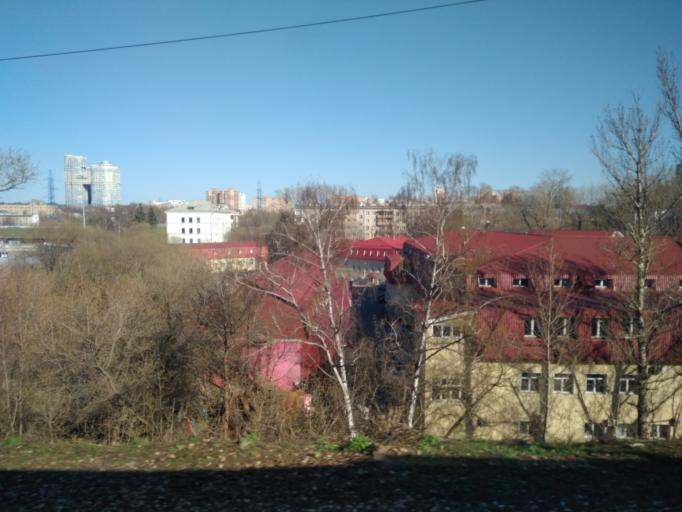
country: RU
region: Moscow
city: Pokrovskoye-Streshnevo
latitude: 55.8189
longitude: 37.4465
